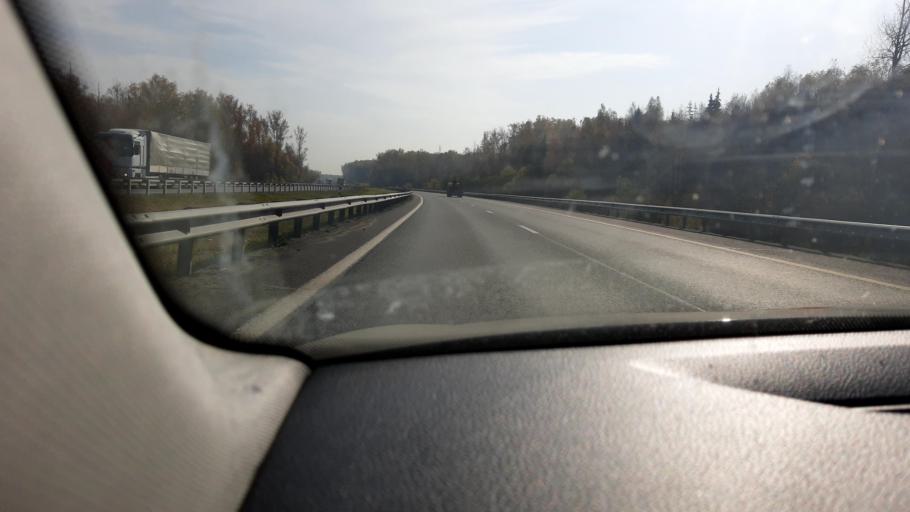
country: RU
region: Moskovskaya
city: Zhilevo
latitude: 55.0225
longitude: 37.9478
